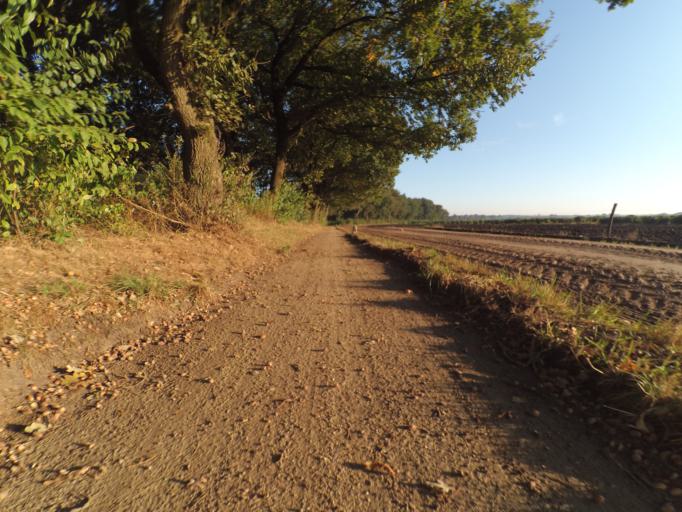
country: NL
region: Gelderland
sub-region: Gemeente Barneveld
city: Garderen
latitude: 52.2348
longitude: 5.7515
